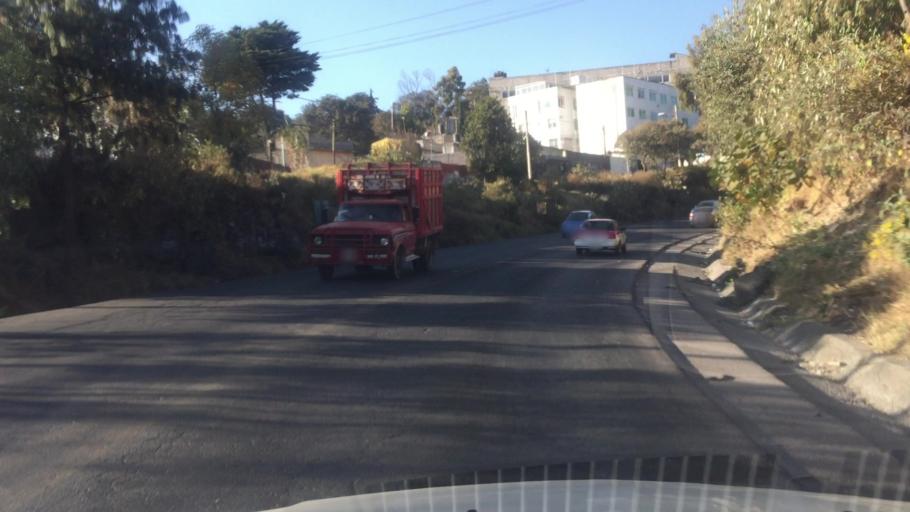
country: MX
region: Mexico City
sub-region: Tlalpan
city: Lomas de Tepemecatl
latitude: 19.2658
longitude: -99.2048
